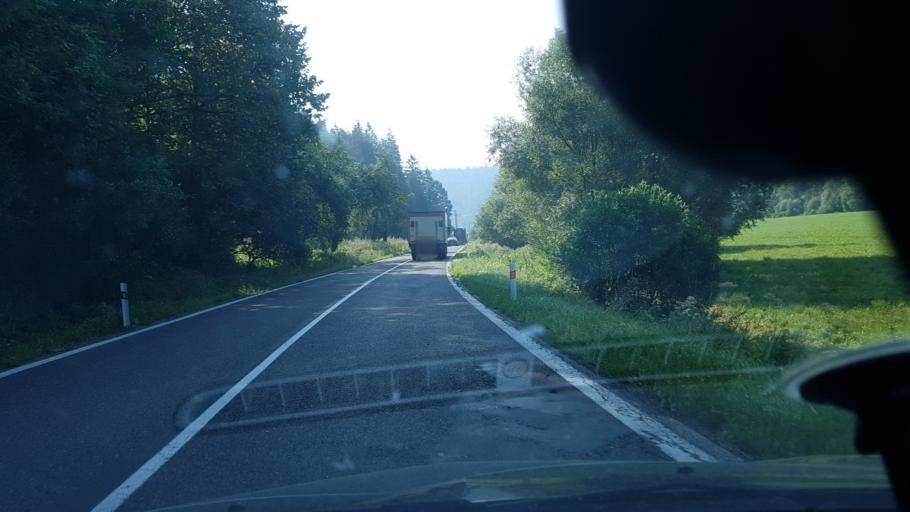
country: SK
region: Zilinsky
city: Tvrdosin
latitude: 49.3007
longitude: 19.4831
